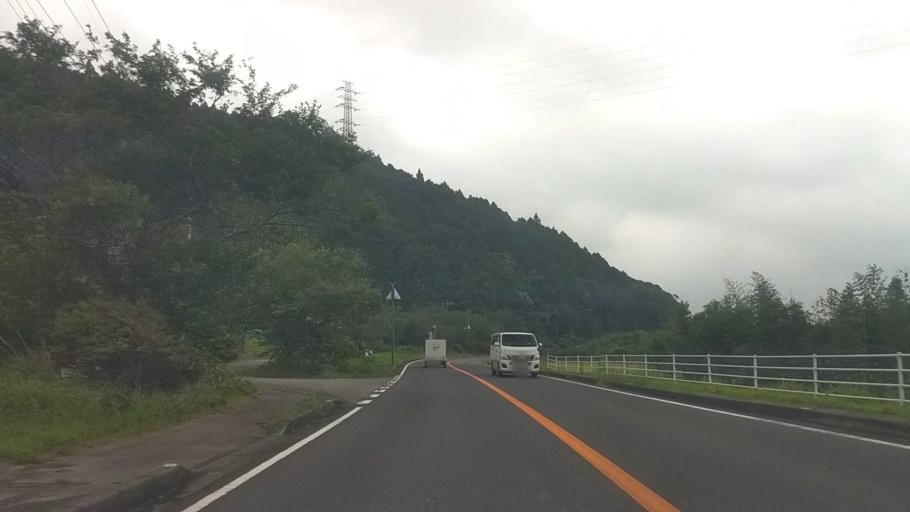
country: JP
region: Chiba
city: Kawaguchi
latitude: 35.1408
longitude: 140.0692
